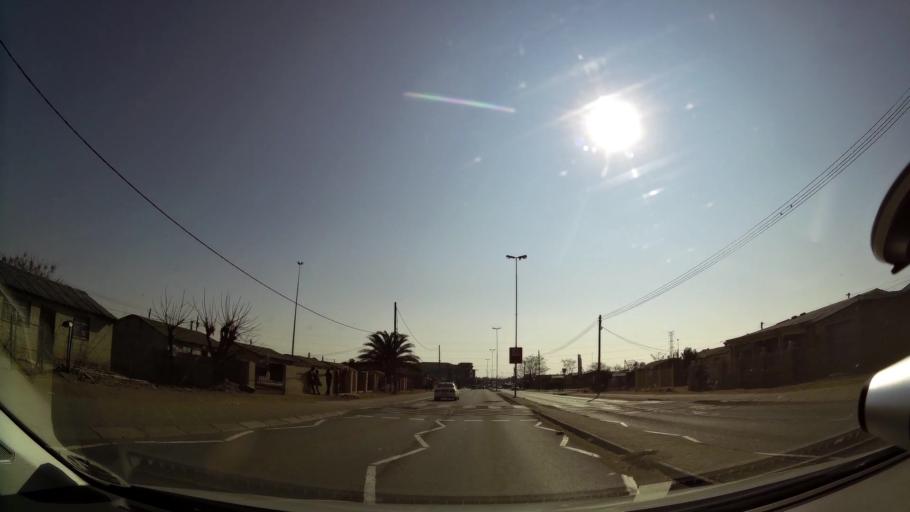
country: ZA
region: Orange Free State
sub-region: Mangaung Metropolitan Municipality
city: Bloemfontein
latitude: -29.1719
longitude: 26.2351
